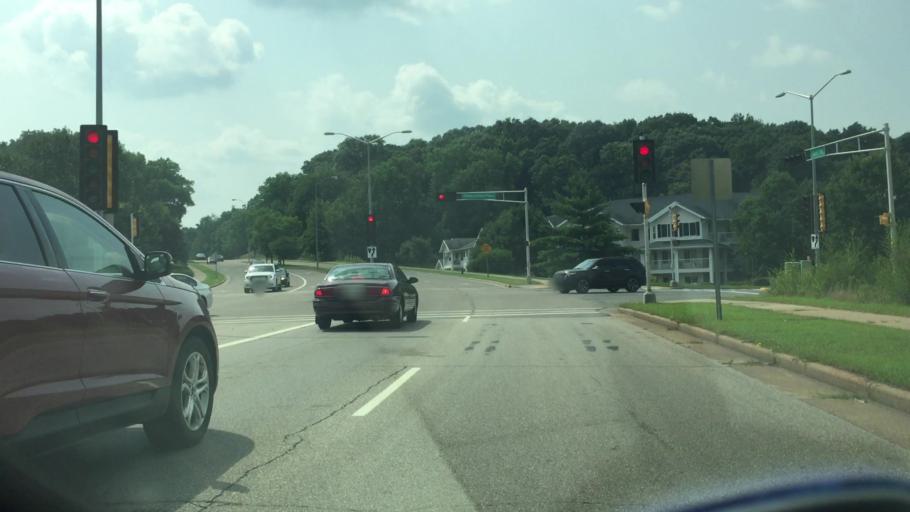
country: US
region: Wisconsin
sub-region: Eau Claire County
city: Altoona
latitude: 44.7719
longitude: -91.4448
